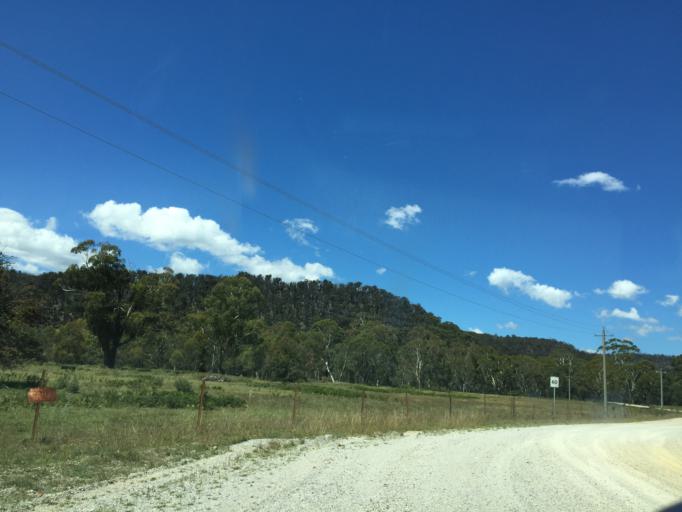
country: AU
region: New South Wales
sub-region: Lithgow
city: Lithgow
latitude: -33.4317
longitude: 150.1350
